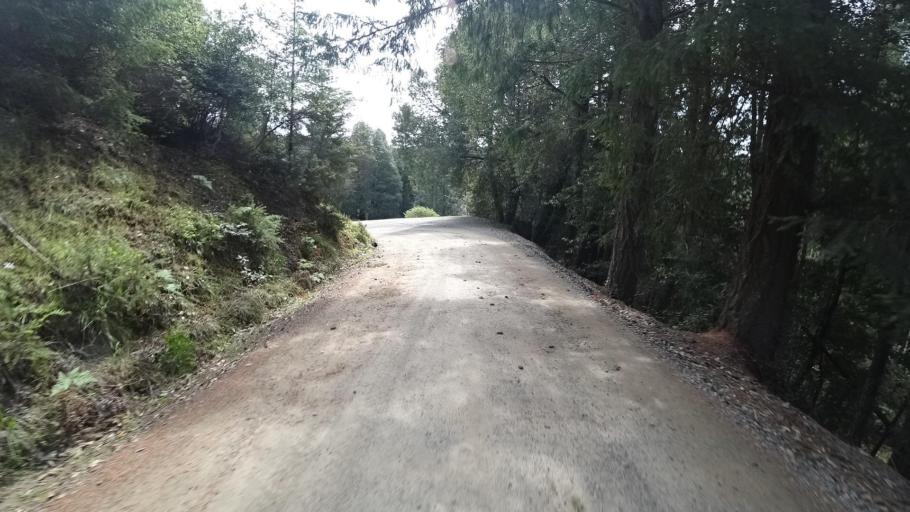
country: US
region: California
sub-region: Humboldt County
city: Redway
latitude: 40.0389
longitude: -123.8472
